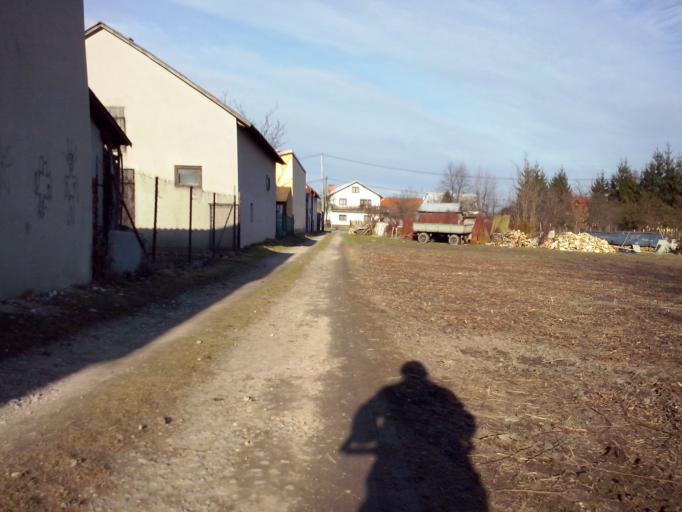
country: PL
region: Subcarpathian Voivodeship
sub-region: Powiat nizanski
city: Krzeszow
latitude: 50.4149
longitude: 22.3490
